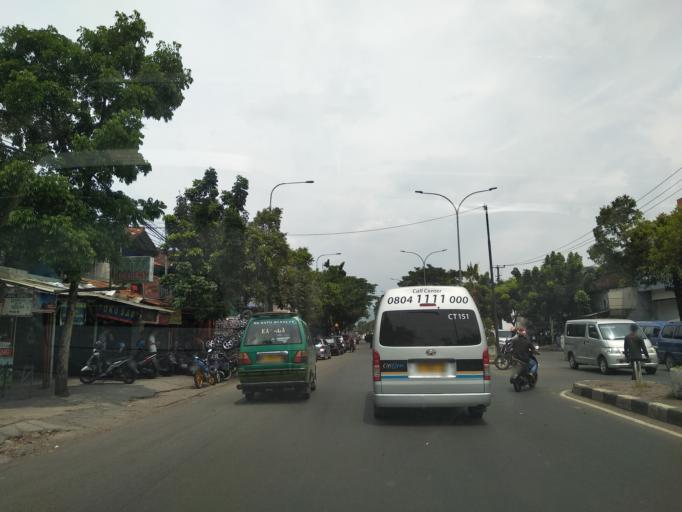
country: ID
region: West Java
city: Bandung
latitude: -6.9607
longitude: 107.6390
